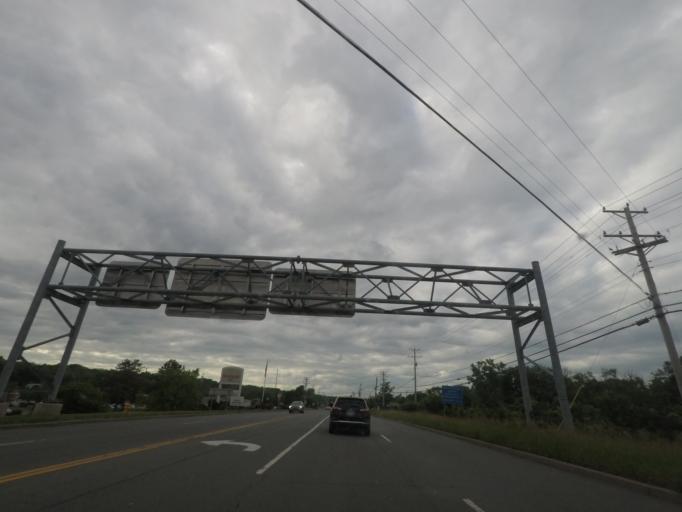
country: US
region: New York
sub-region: Orange County
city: Gardnertown
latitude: 41.5171
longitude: -74.0681
